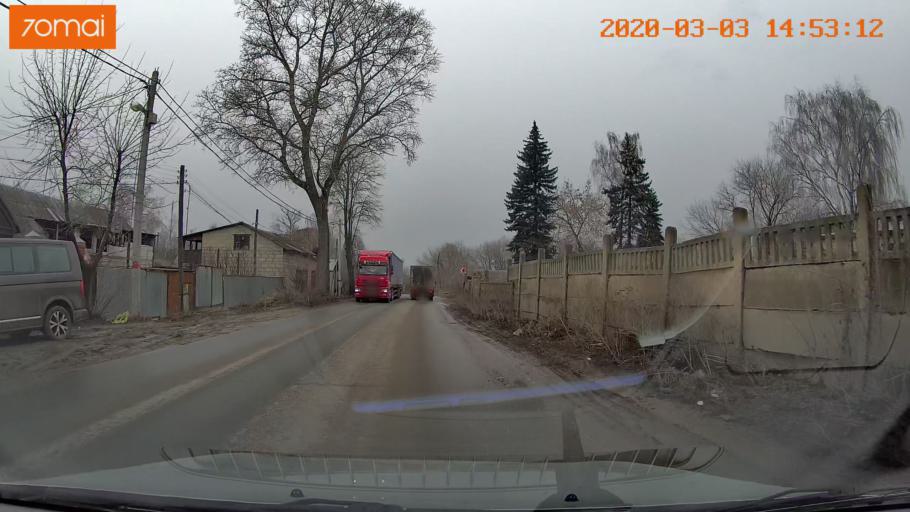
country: RU
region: Moskovskaya
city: Korenevo
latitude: 55.6739
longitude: 38.0110
